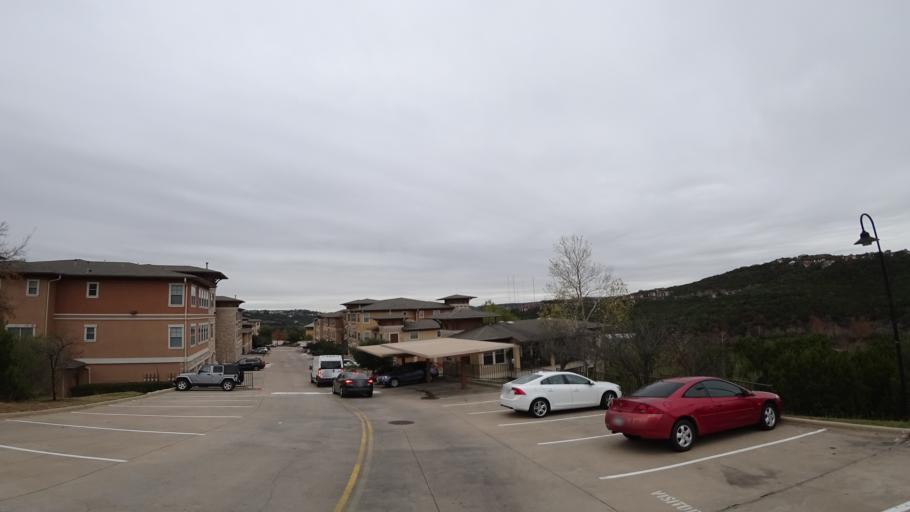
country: US
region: Texas
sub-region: Travis County
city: West Lake Hills
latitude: 30.3654
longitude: -97.7929
